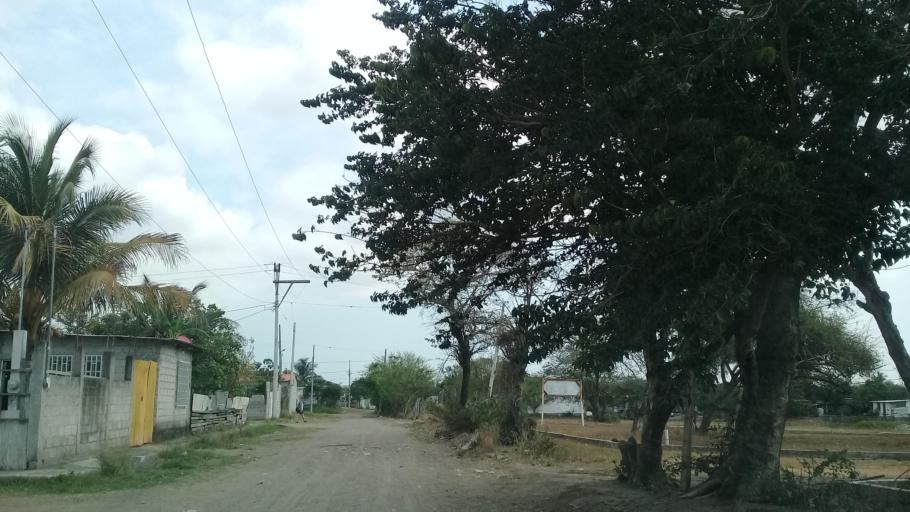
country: MX
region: Veracruz
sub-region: Veracruz
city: Las Amapolas
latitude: 19.1335
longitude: -96.2316
